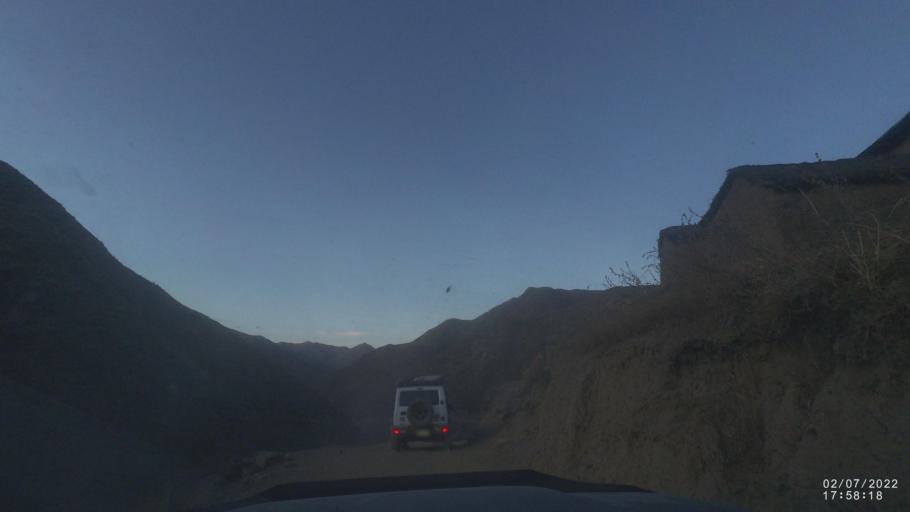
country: BO
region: Cochabamba
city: Irpa Irpa
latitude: -17.8415
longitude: -66.6174
